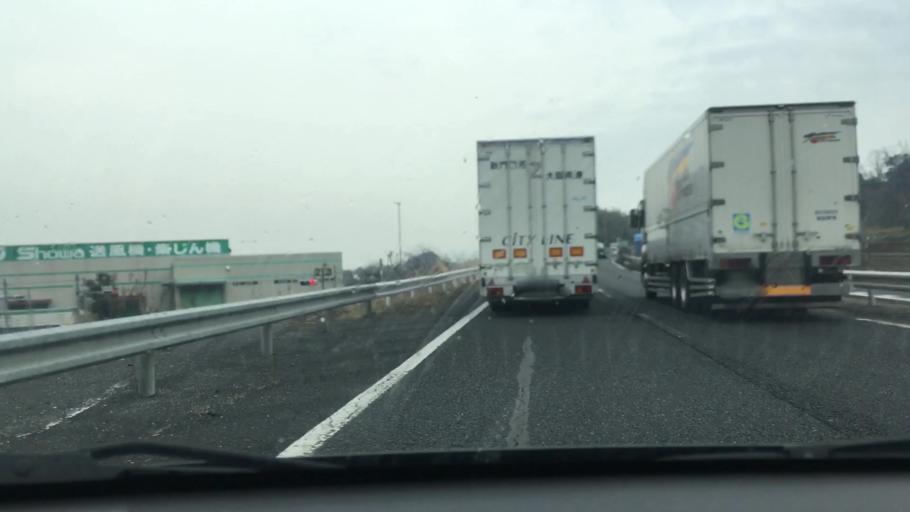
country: JP
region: Mie
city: Ueno-ebisumachi
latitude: 34.8176
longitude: 136.2151
